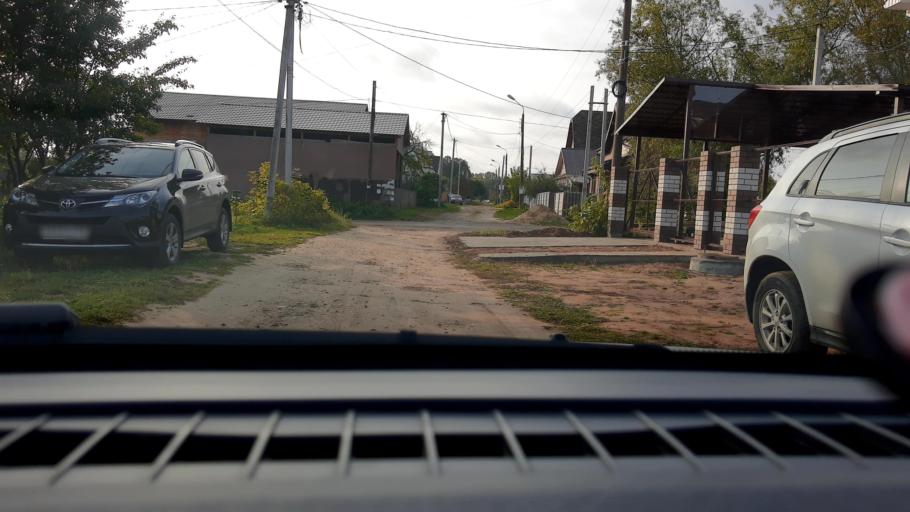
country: RU
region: Nizjnij Novgorod
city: Kstovo
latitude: 56.1881
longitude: 44.1607
